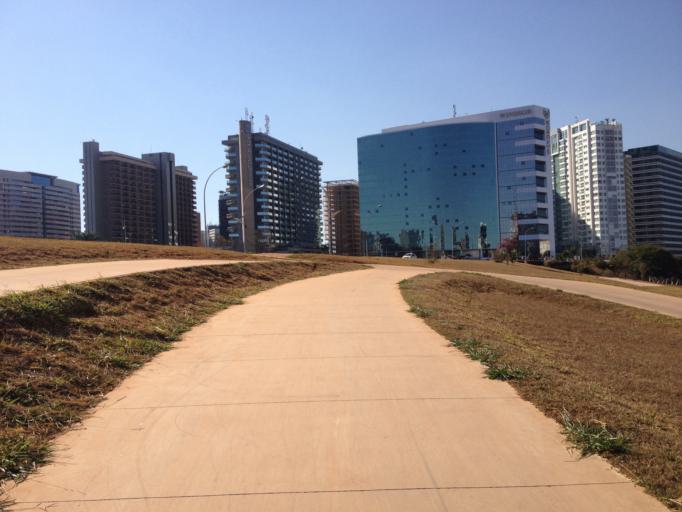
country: BR
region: Federal District
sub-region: Brasilia
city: Brasilia
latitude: -15.7933
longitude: -47.8855
